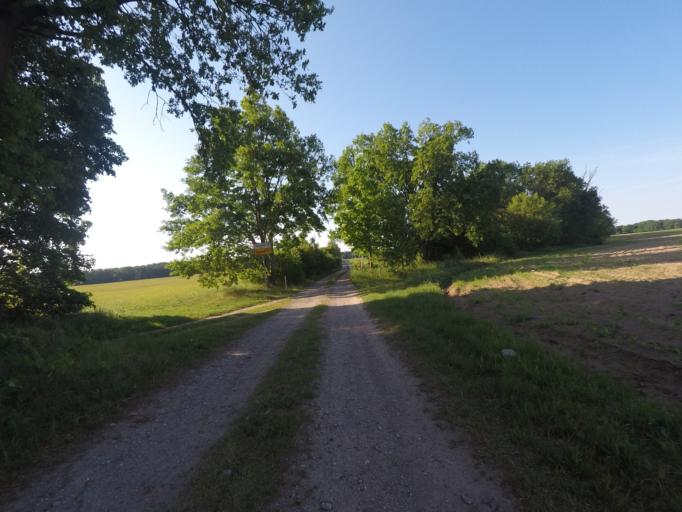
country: DE
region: Brandenburg
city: Joachimsthal
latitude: 52.8955
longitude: 13.7051
